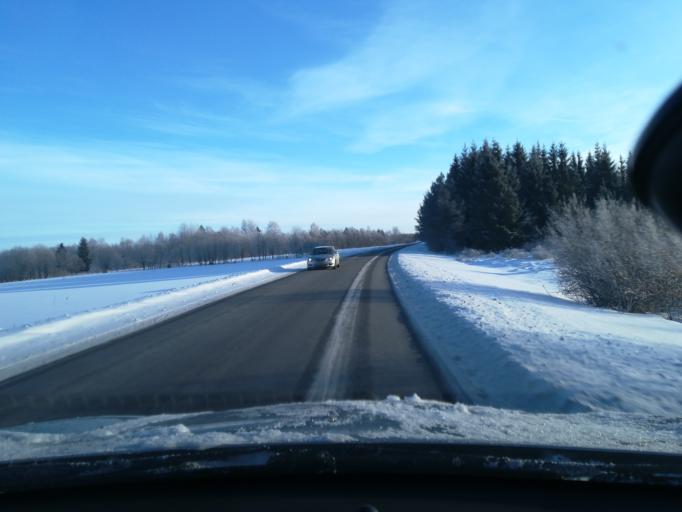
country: EE
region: Harju
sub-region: Keila linn
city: Keila
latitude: 59.3803
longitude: 24.4510
